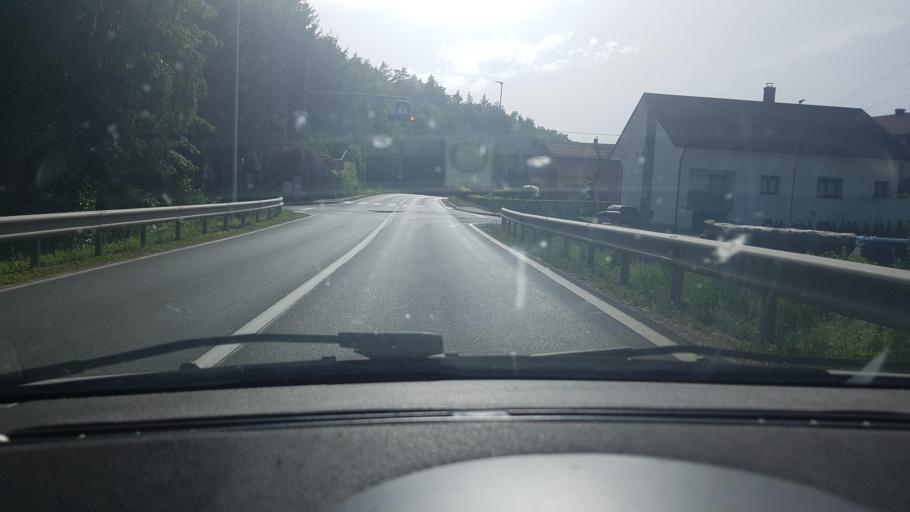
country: SI
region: Rogaska Slatina
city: Rogaska Slatina
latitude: 46.2520
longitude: 15.6300
